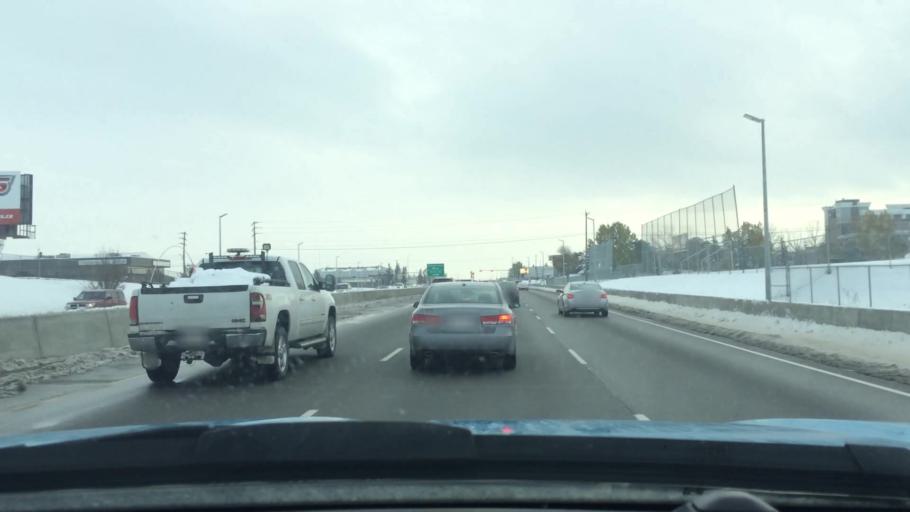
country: CA
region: Alberta
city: Calgary
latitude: 51.0927
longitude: -114.0169
